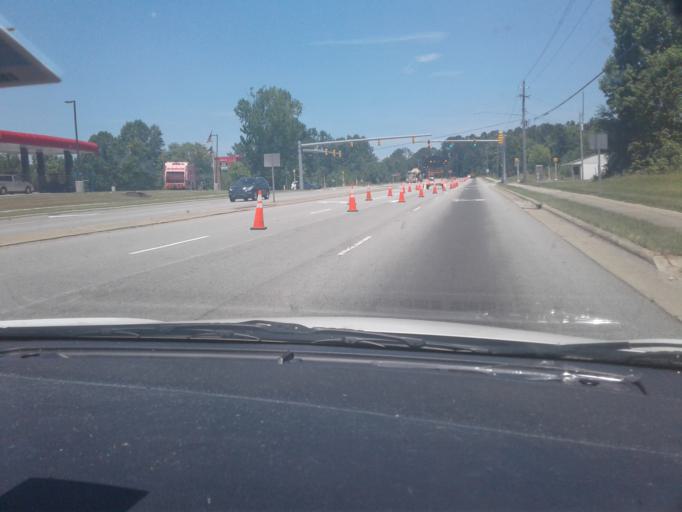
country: US
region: North Carolina
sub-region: Wake County
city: Fuquay-Varina
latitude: 35.6100
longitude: -78.8069
